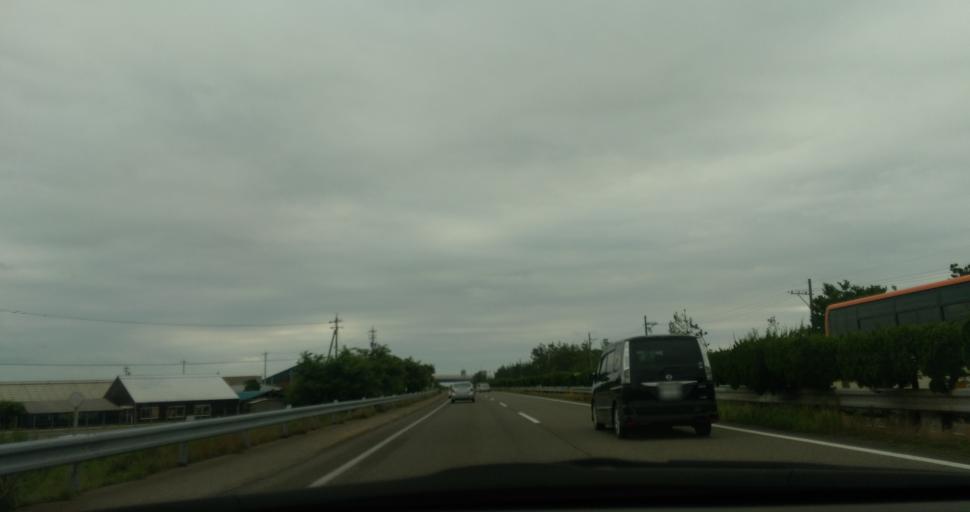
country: JP
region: Ishikawa
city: Matsuto
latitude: 36.5391
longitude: 136.5333
